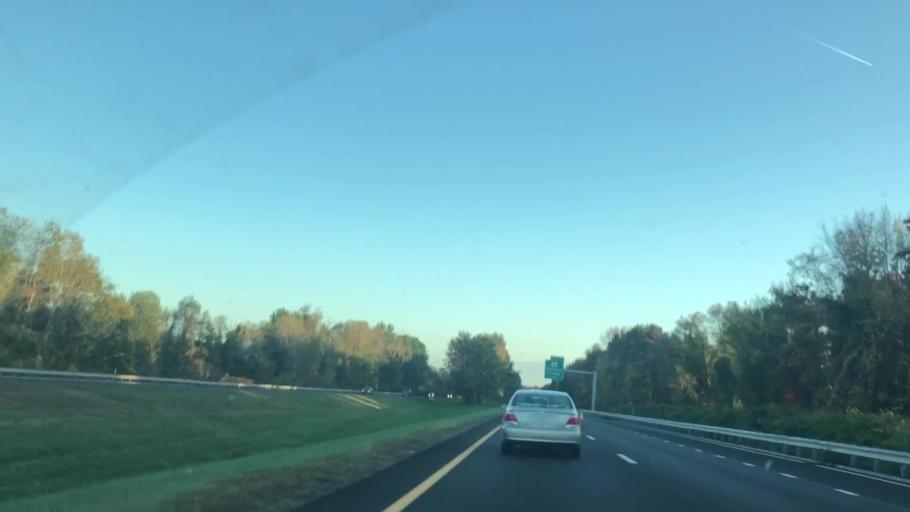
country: US
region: Massachusetts
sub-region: Franklin County
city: South Deerfield
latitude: 42.5021
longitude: -72.6195
